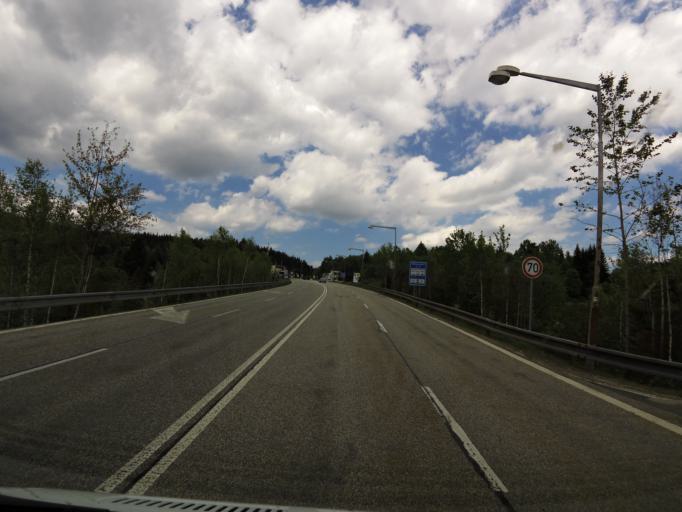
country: DE
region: Bavaria
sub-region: Lower Bavaria
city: Philippsreut
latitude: 48.8819
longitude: 13.7045
